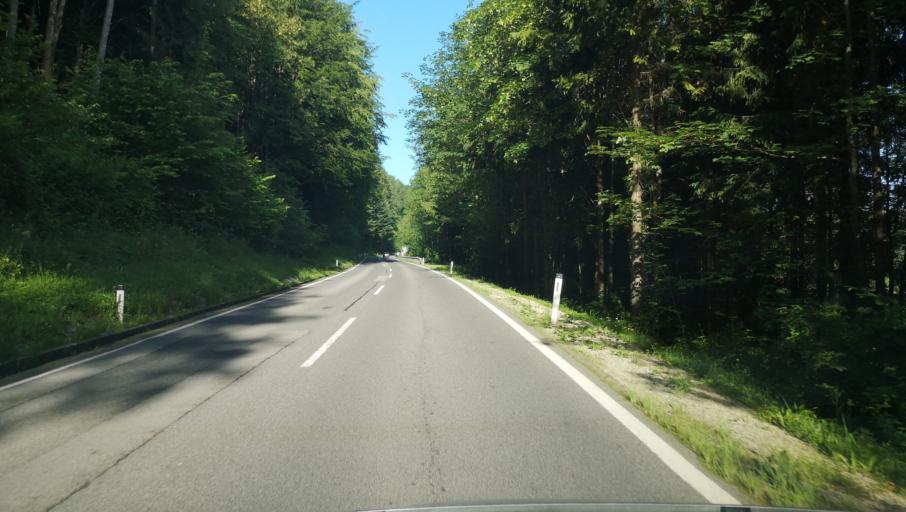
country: AT
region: Lower Austria
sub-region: Politischer Bezirk Scheibbs
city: Randegg
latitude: 47.9725
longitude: 14.9845
